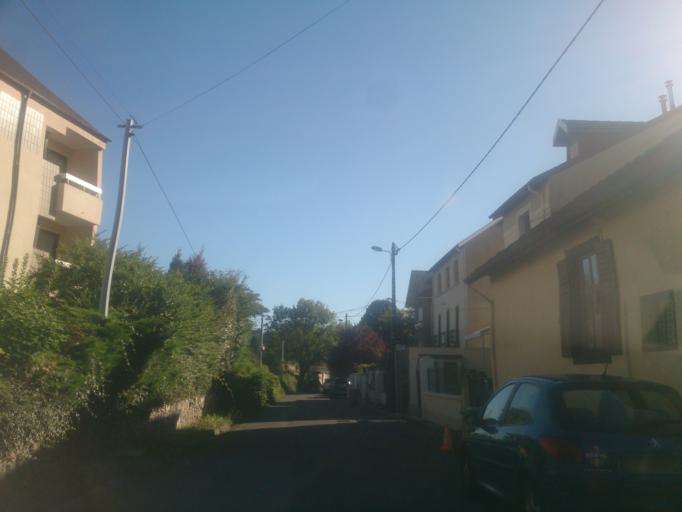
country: FR
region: Midi-Pyrenees
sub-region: Departement des Hautes-Pyrenees
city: Bagneres-de-Bigorre
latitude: 43.0694
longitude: 0.1500
